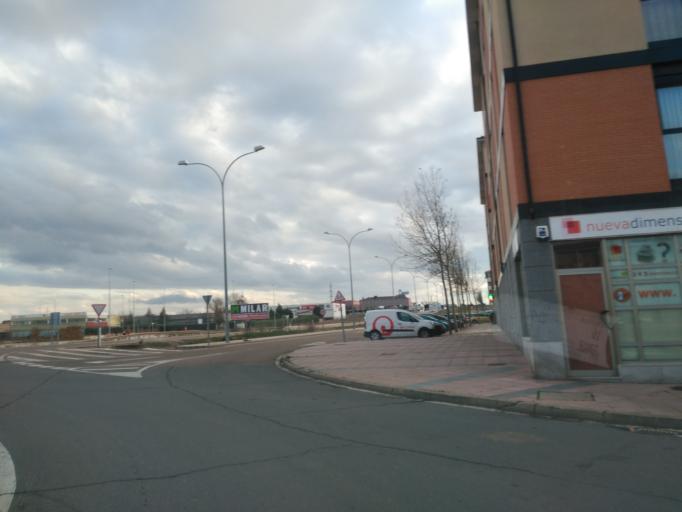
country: ES
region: Castille and Leon
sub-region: Provincia de Salamanca
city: Carbajosa de la Sagrada
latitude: 40.9447
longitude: -5.6698
